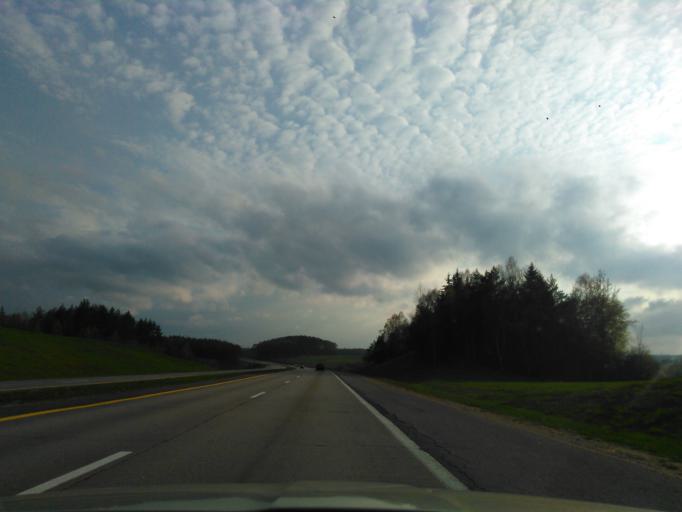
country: BY
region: Minsk
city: Astrashytski Haradok
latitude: 54.0694
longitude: 27.7223
